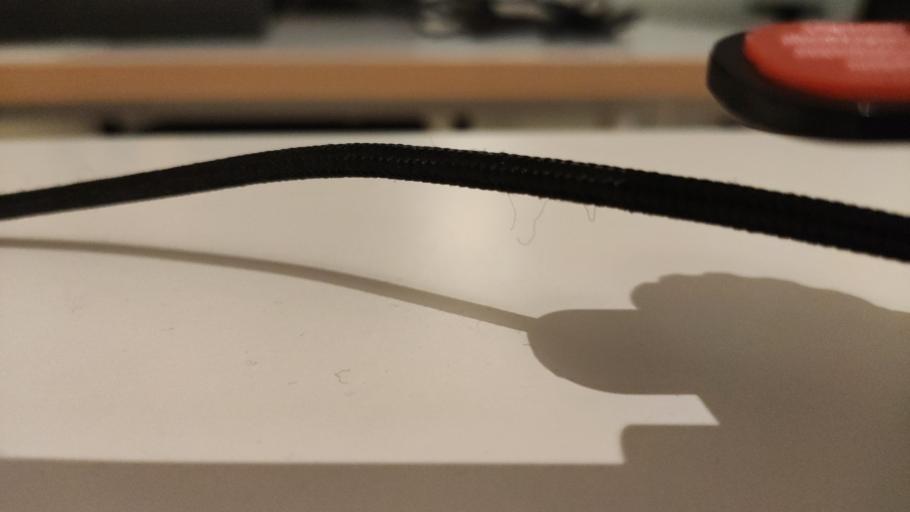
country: RU
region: Moskovskaya
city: Il'inskiy Pogost
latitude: 55.5168
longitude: 38.8716
